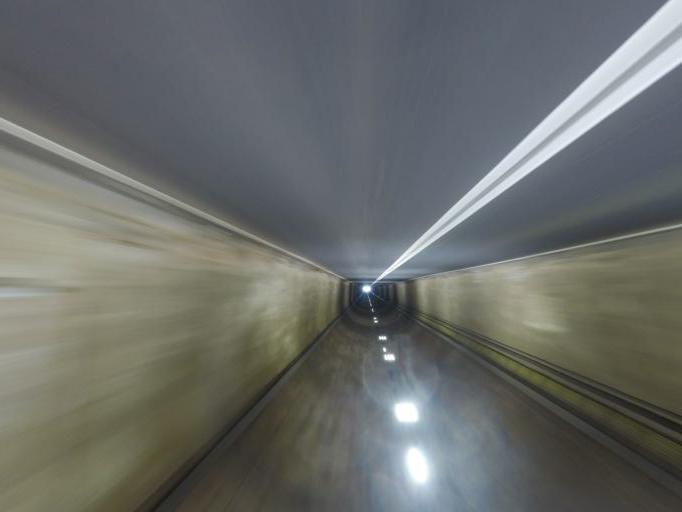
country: ES
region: Canary Islands
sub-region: Provincia de Santa Cruz de Tenerife
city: Hermigua
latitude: 28.1339
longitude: -17.1898
